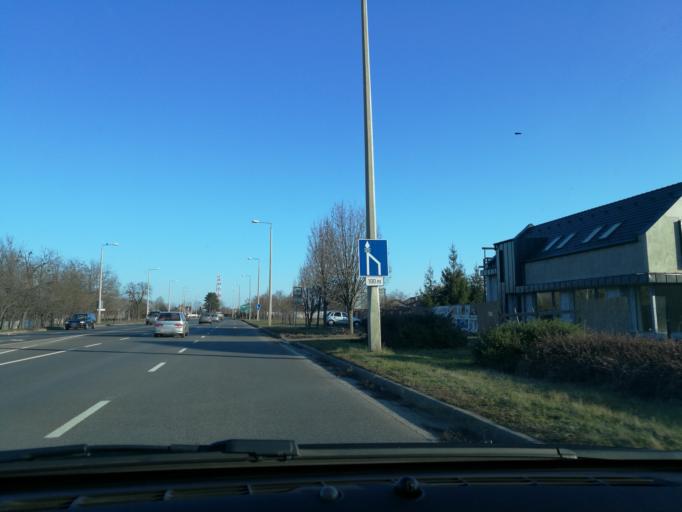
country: HU
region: Szabolcs-Szatmar-Bereg
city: Nyirpazony
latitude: 47.9496
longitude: 21.7835
